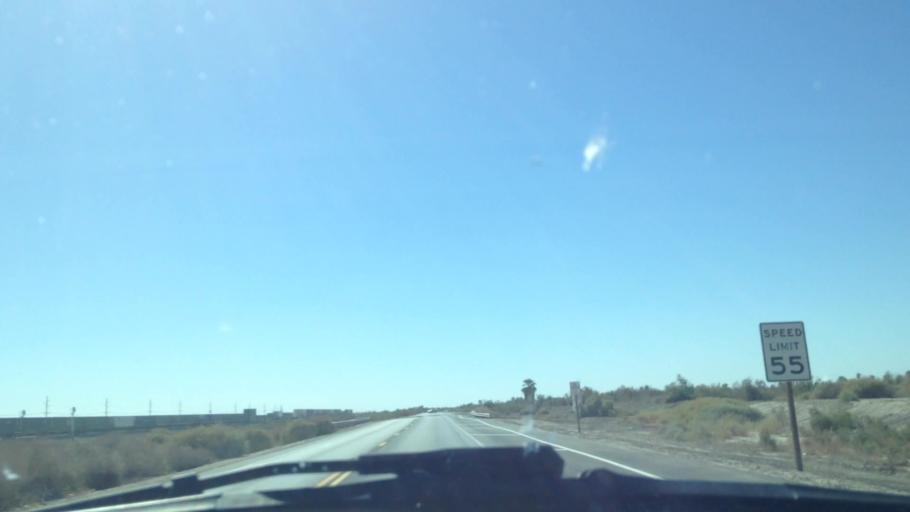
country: US
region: California
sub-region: Riverside County
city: Mecca
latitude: 33.5655
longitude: -116.0754
